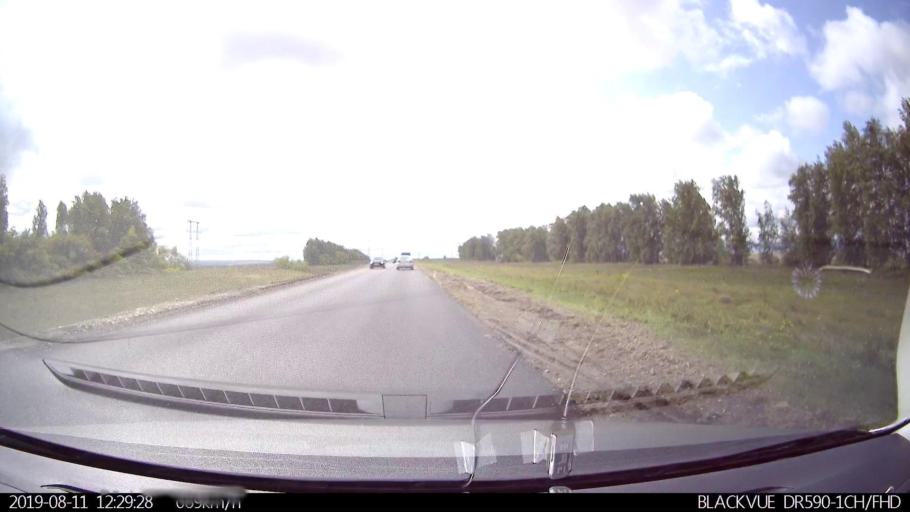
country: RU
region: Ulyanovsk
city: Ignatovka
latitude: 53.8343
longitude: 47.9023
